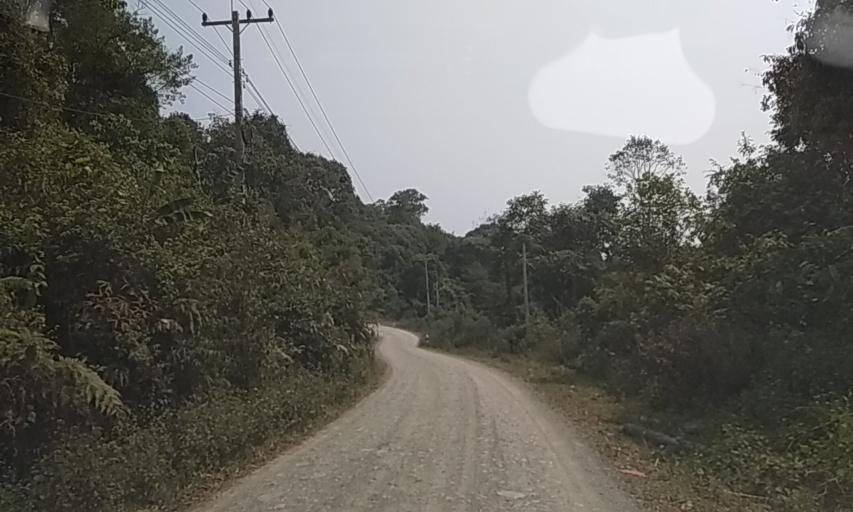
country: TH
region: Nan
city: Chaloem Phra Kiat
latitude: 20.0352
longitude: 101.0941
